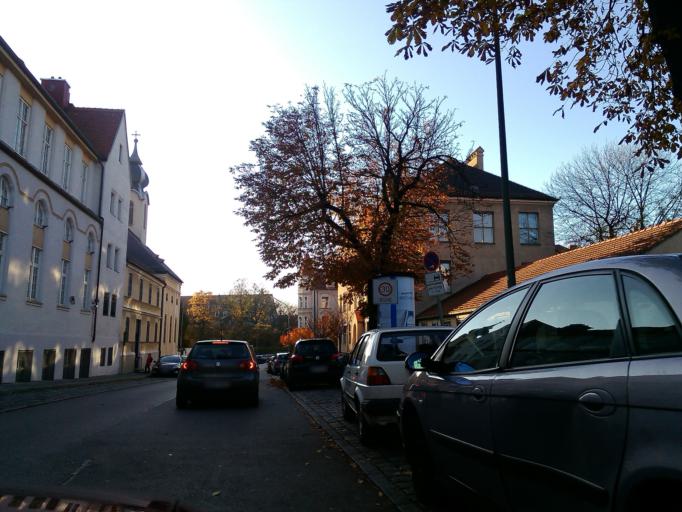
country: DE
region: Bavaria
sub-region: Upper Bavaria
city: Pasing
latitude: 48.1460
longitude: 11.4589
